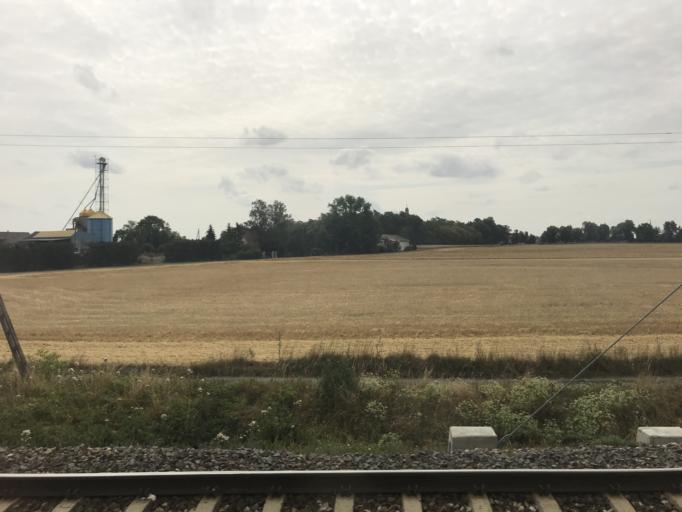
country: PL
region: Kujawsko-Pomorskie
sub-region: Powiat mogilenski
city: Mogilno
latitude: 52.7100
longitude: 18.0294
